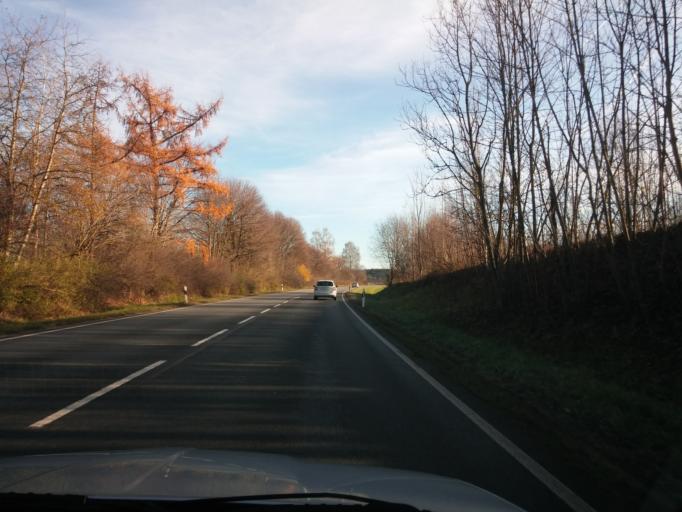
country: DE
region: Bavaria
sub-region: Upper Bavaria
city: Babensham
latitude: 48.0562
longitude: 12.2750
